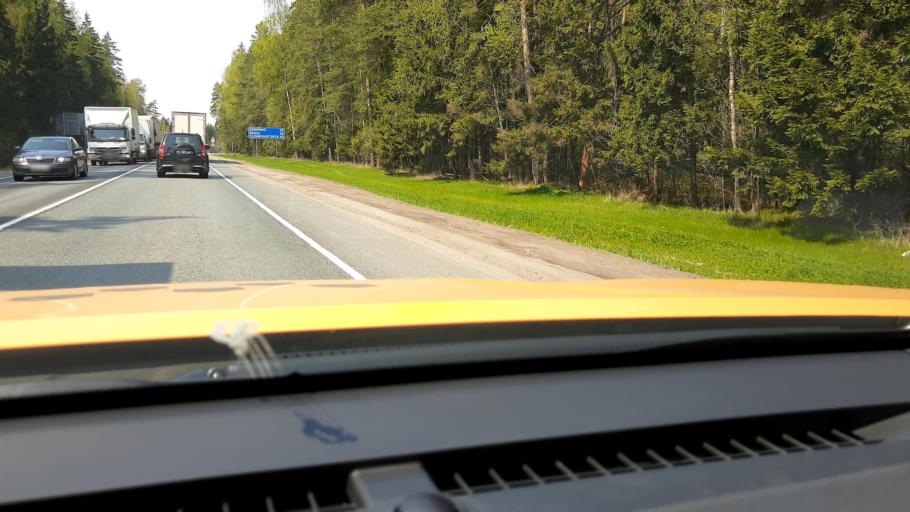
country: RU
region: Moskovskaya
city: Chernogolovka
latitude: 55.9865
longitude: 38.3358
